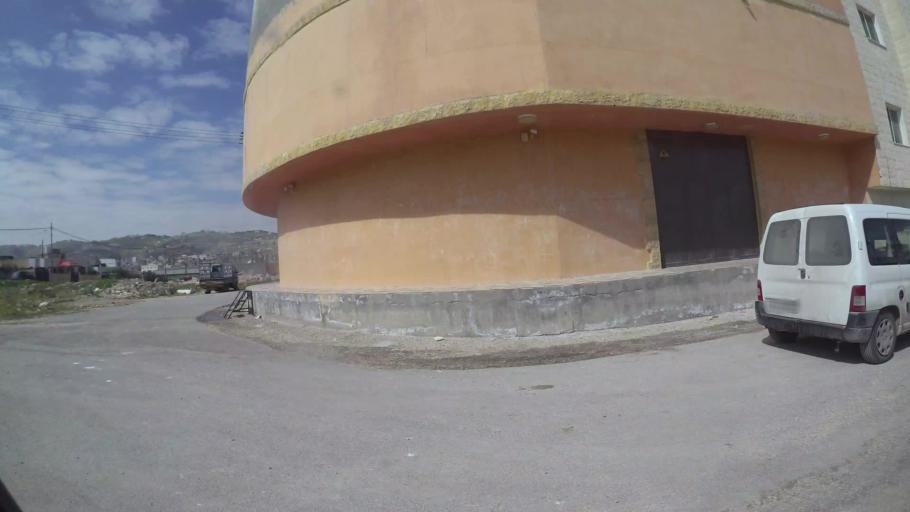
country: JO
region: Amman
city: Al Jubayhah
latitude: 32.0625
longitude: 35.8242
